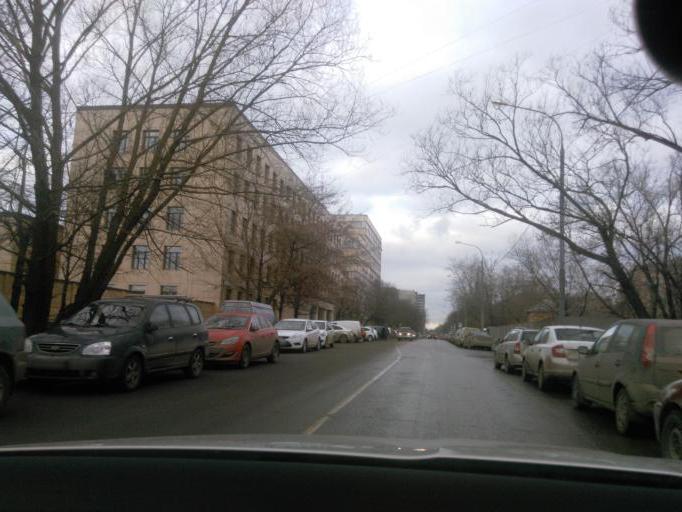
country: RU
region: Moskovskaya
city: Koptevo
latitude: 55.8162
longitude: 37.5300
